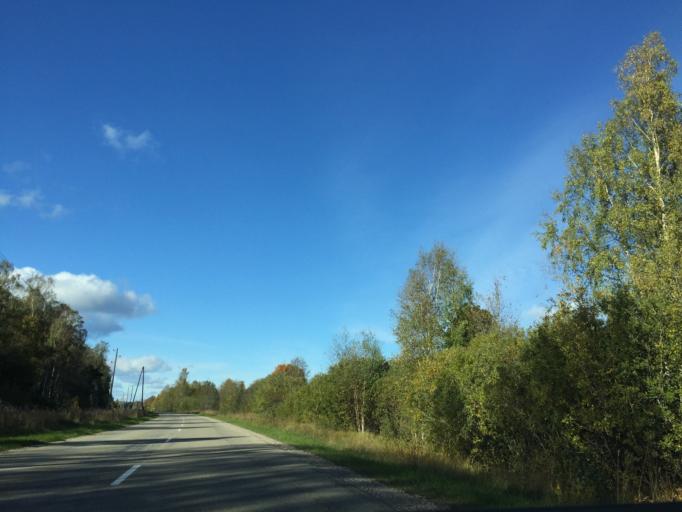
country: LV
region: Rojas
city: Roja
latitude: 57.4460
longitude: 22.9009
